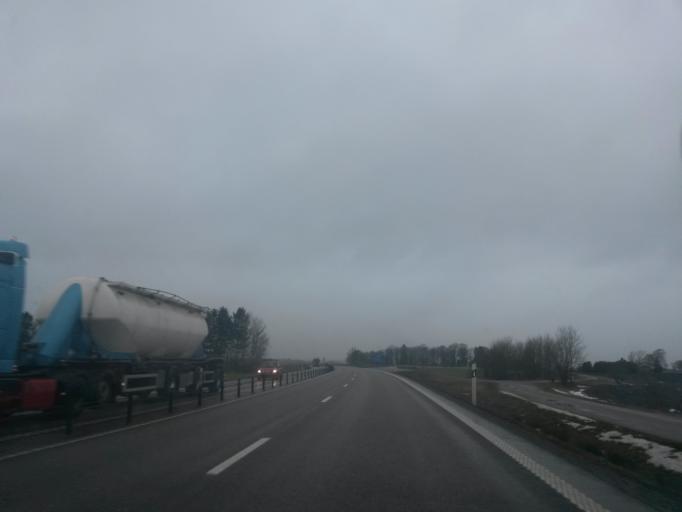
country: SE
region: Vaestra Goetaland
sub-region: Vanersborgs Kommun
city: Vargon
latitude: 58.2928
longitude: 12.3890
